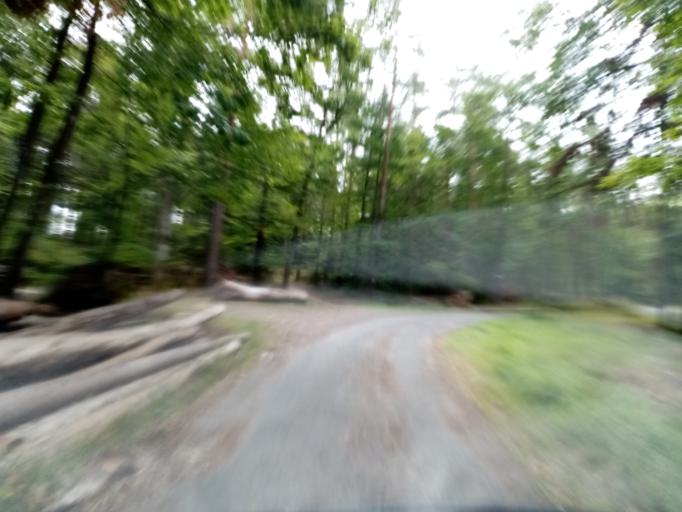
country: FR
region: Alsace
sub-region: Departement du Bas-Rhin
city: Dambach-la-Ville
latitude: 48.3365
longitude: 7.3919
